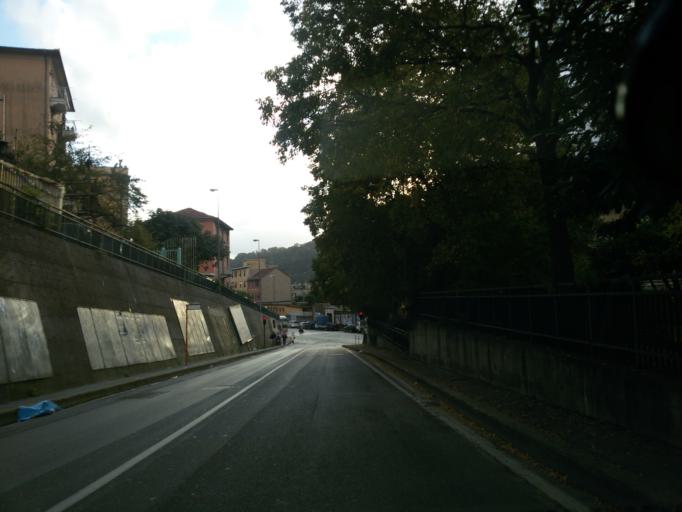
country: IT
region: Liguria
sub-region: Provincia di Genova
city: Genoa
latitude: 44.4532
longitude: 8.8961
